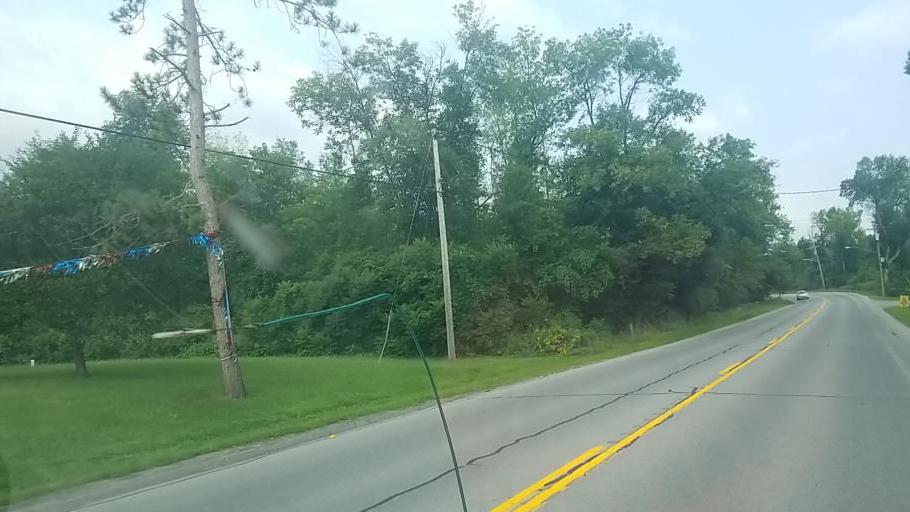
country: US
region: New York
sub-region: Montgomery County
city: Fort Plain
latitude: 42.9254
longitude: -74.6031
